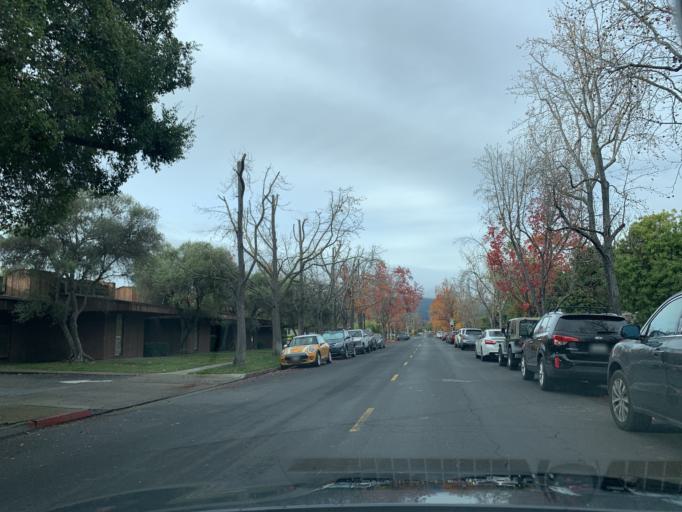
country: US
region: California
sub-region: Santa Clara County
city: Cambrian Park
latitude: 37.2474
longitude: -121.9509
